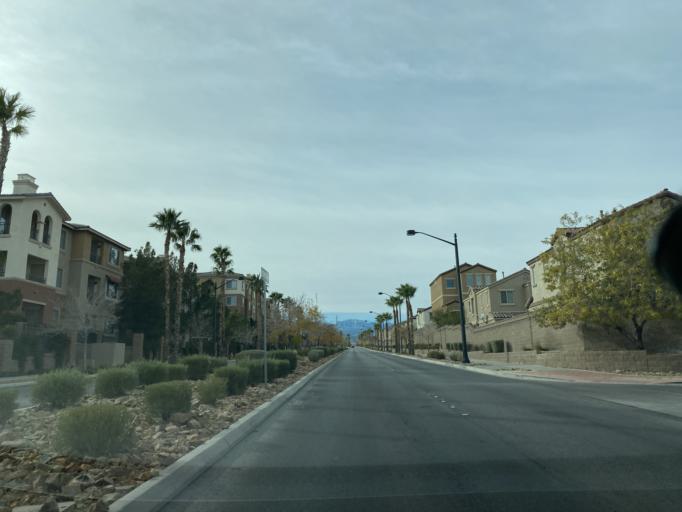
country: US
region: Nevada
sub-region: Clark County
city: Summerlin South
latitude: 36.2992
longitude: -115.2903
